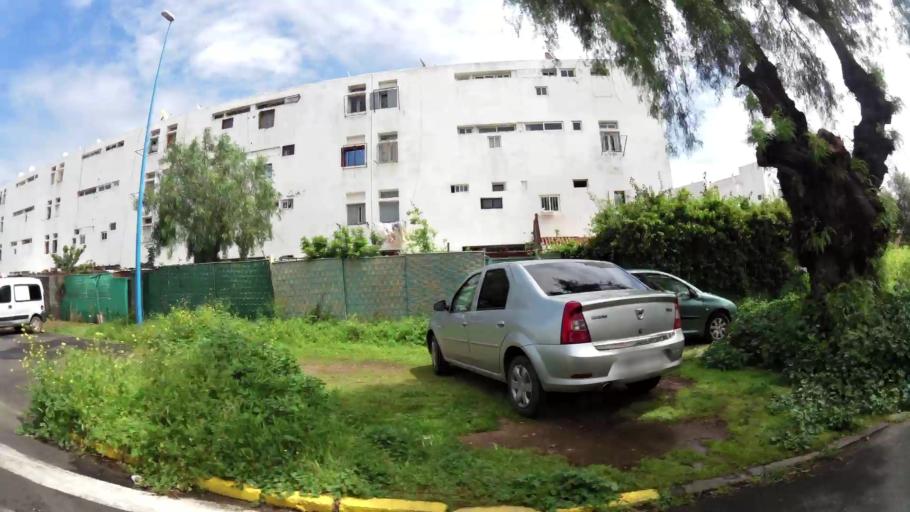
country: MA
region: Grand Casablanca
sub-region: Casablanca
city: Casablanca
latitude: 33.5667
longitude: -7.6347
